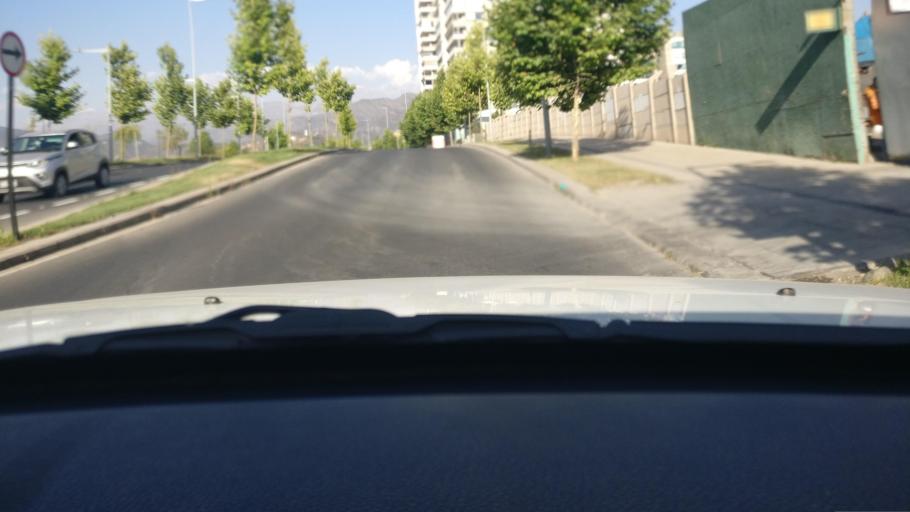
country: CL
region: Santiago Metropolitan
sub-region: Provincia de Santiago
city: Villa Presidente Frei, Nunoa, Santiago, Chile
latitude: -33.3719
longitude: -70.5214
